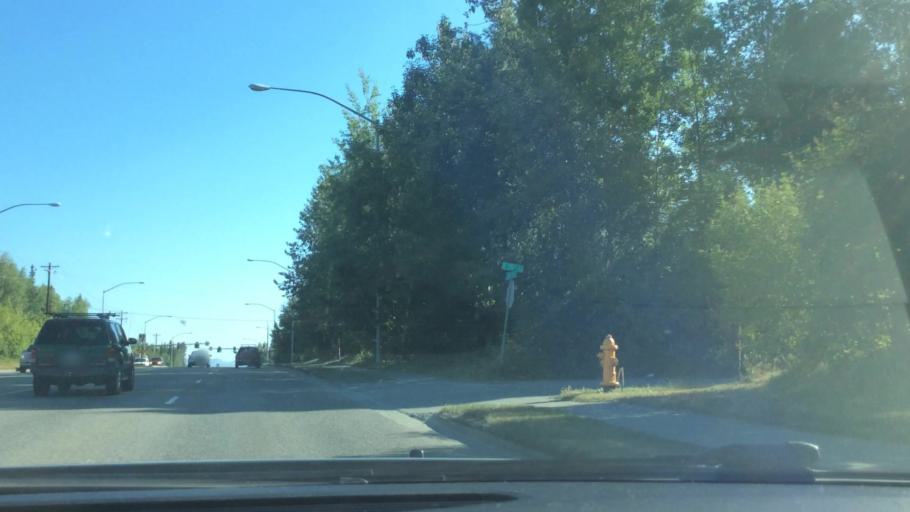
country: US
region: Alaska
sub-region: Anchorage Municipality
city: Anchorage
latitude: 61.1576
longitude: -149.8344
